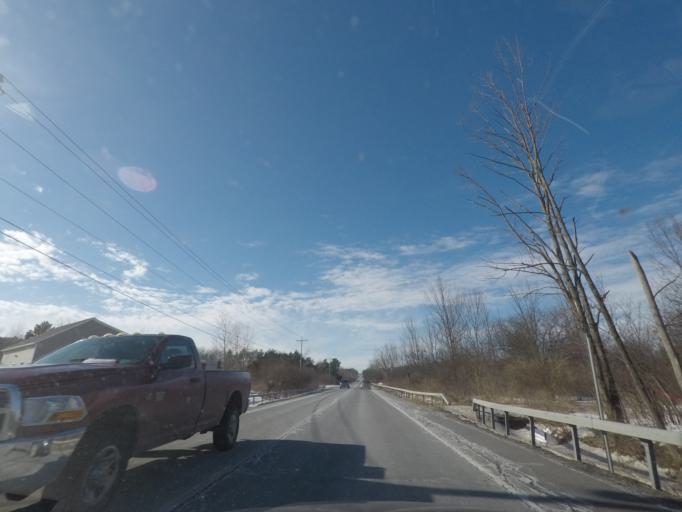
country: US
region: New York
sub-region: Albany County
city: Altamont
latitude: 42.7432
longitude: -74.0259
